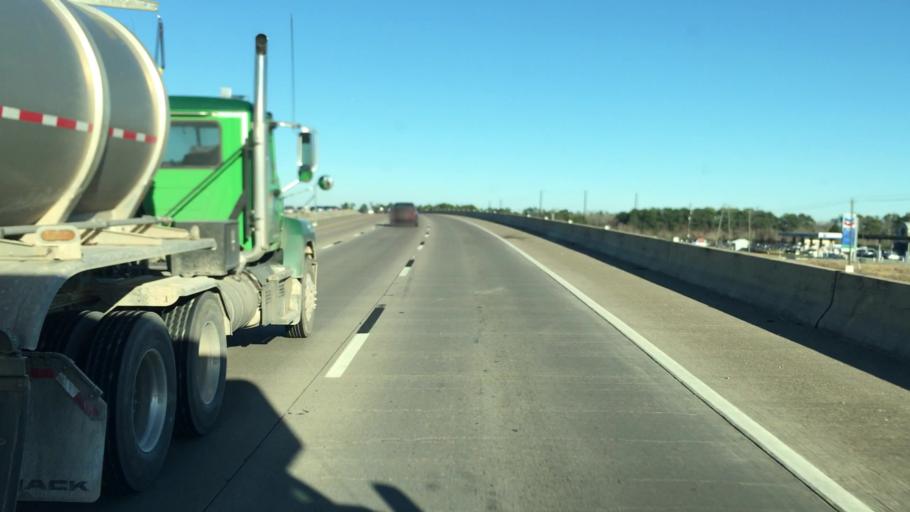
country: US
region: Texas
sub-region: Chambers County
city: Mont Belvieu
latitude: 29.8116
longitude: -94.9412
